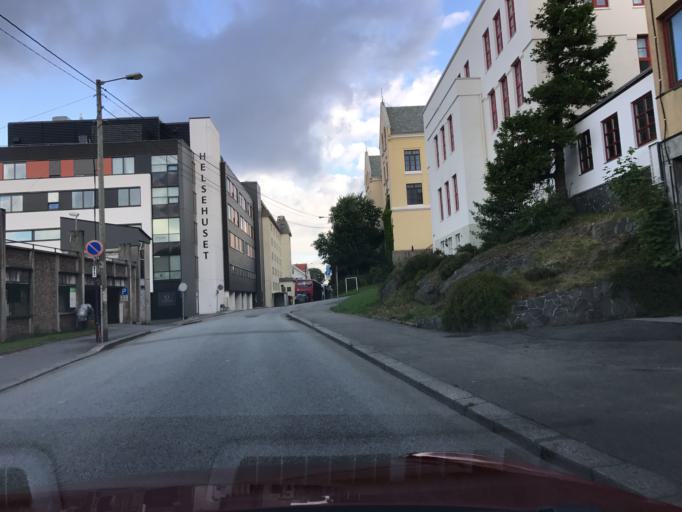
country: NO
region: Rogaland
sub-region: Haugesund
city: Haugesund
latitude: 59.4114
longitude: 5.2734
